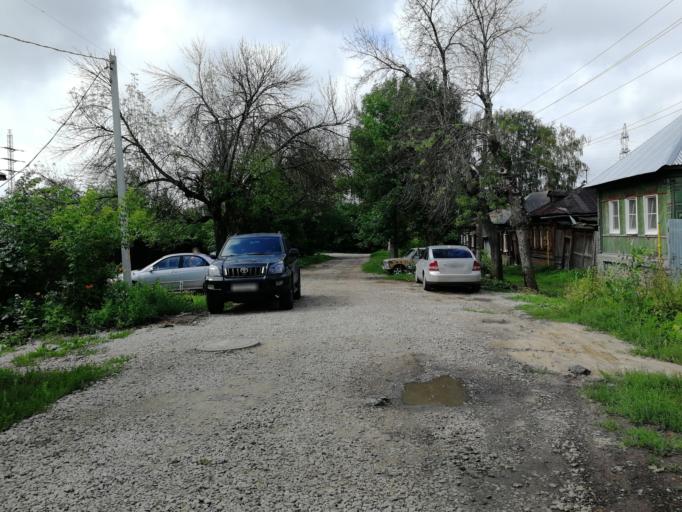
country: RU
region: Tula
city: Tula
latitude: 54.1979
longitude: 37.6317
